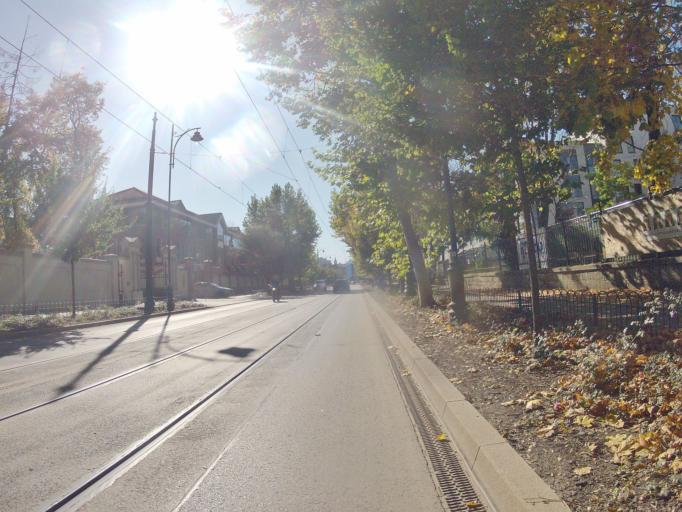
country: PL
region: Lesser Poland Voivodeship
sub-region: Krakow
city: Krakow
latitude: 50.0702
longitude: 19.9540
